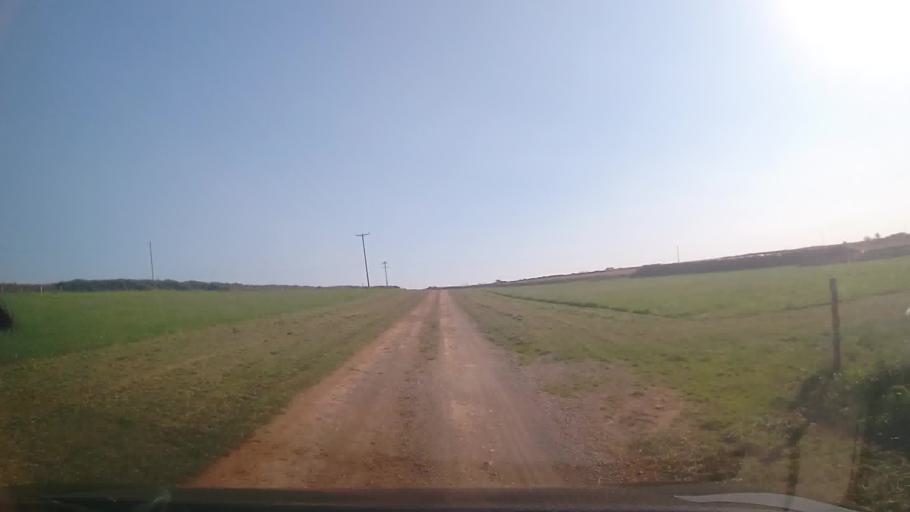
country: GB
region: Wales
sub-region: Pembrokeshire
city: Llanrhian
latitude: 51.9247
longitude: -5.2193
